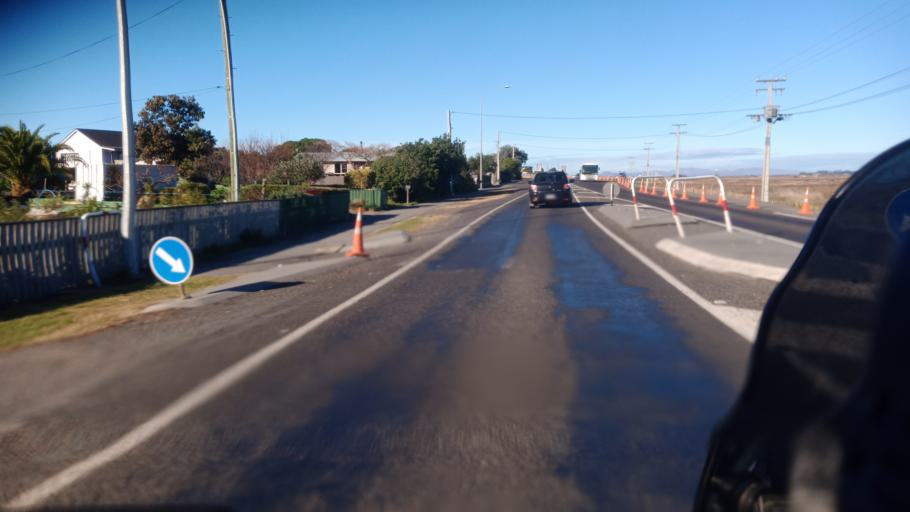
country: NZ
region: Hawke's Bay
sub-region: Napier City
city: Napier
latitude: -39.4394
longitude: 176.8706
